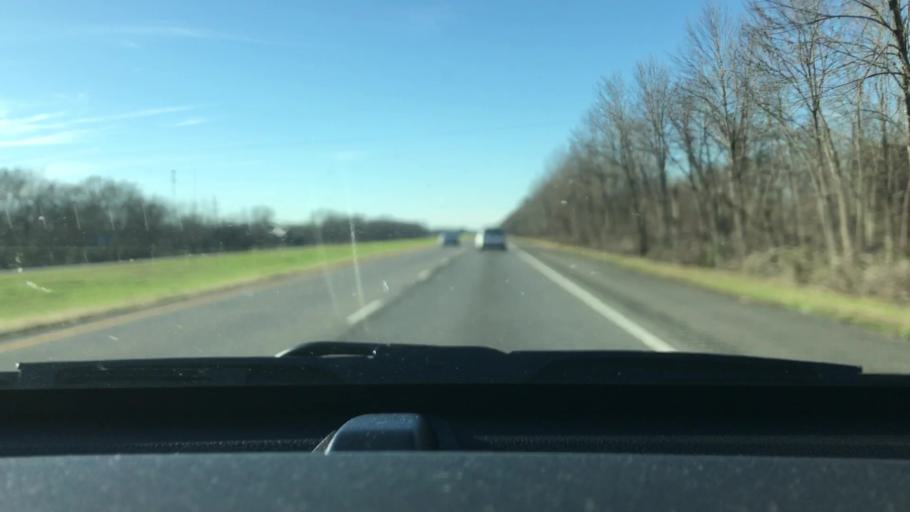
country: US
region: Louisiana
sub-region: Rapides Parish
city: Boyce
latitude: 31.3748
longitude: -92.6359
